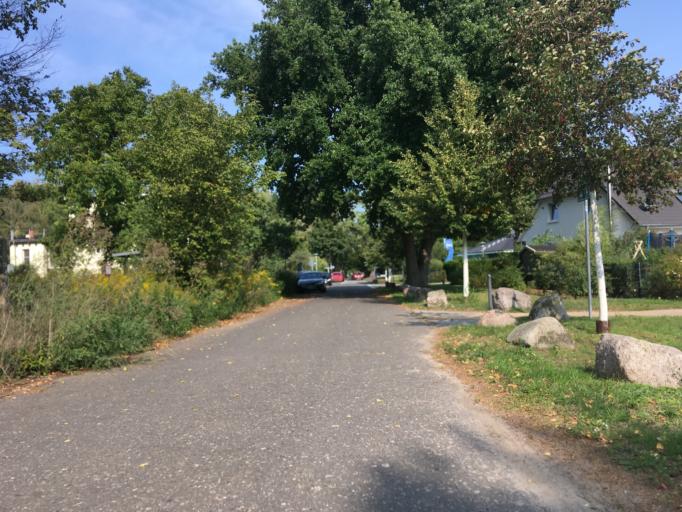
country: DE
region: Berlin
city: Konradshohe
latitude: 52.6004
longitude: 13.1970
